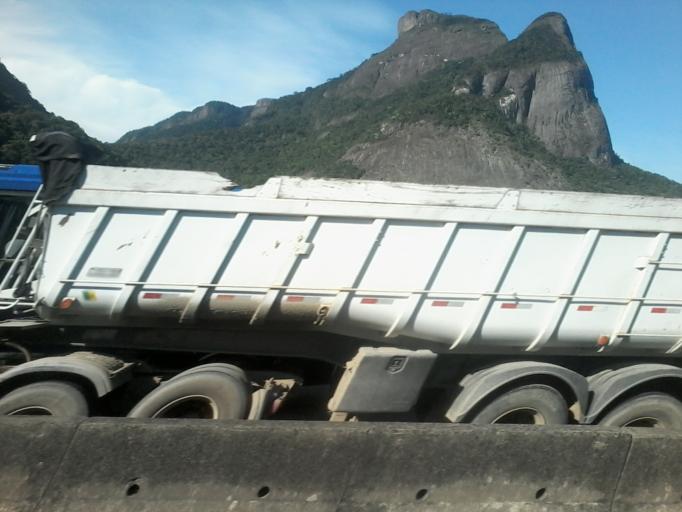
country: BR
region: Rio de Janeiro
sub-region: Rio De Janeiro
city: Rio de Janeiro
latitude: -23.0110
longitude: -43.3013
